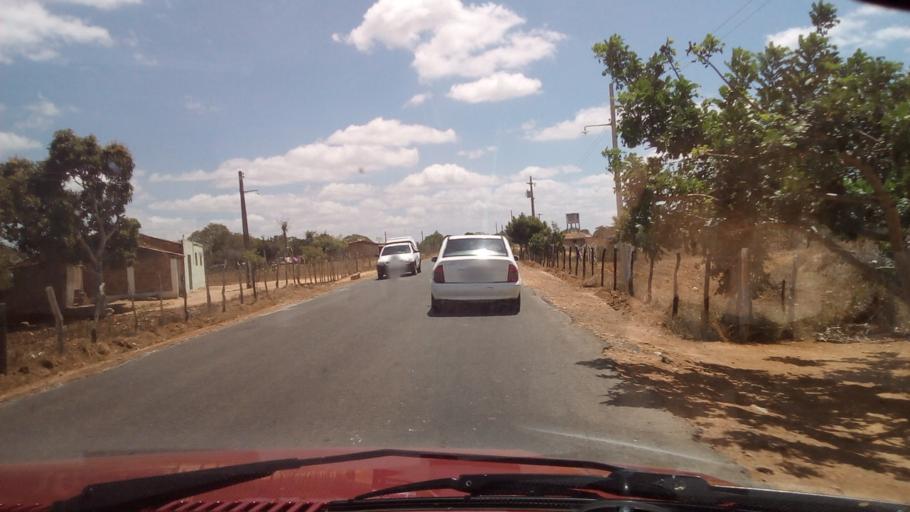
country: BR
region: Paraiba
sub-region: Cacimba De Dentro
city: Cacimba de Dentro
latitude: -6.6000
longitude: -35.8116
